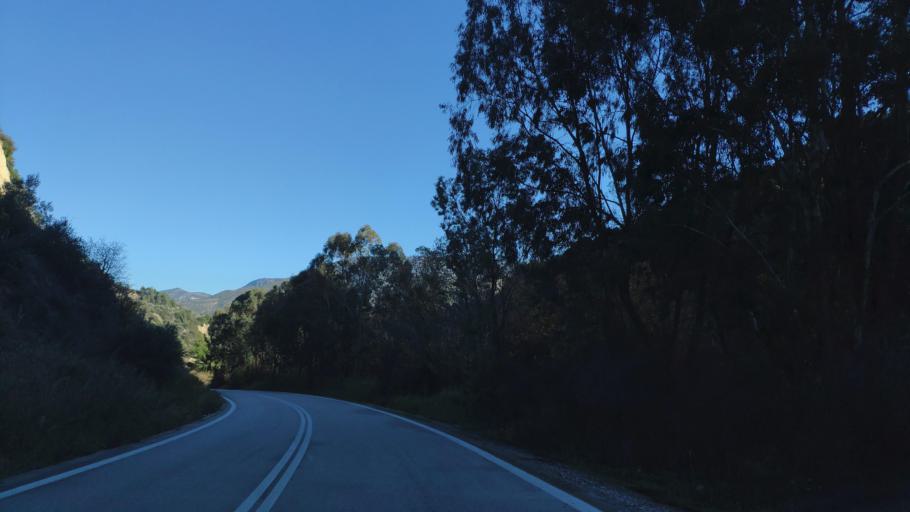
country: GR
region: Peloponnese
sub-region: Nomos Korinthias
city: Xylokastro
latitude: 38.0089
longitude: 22.5220
